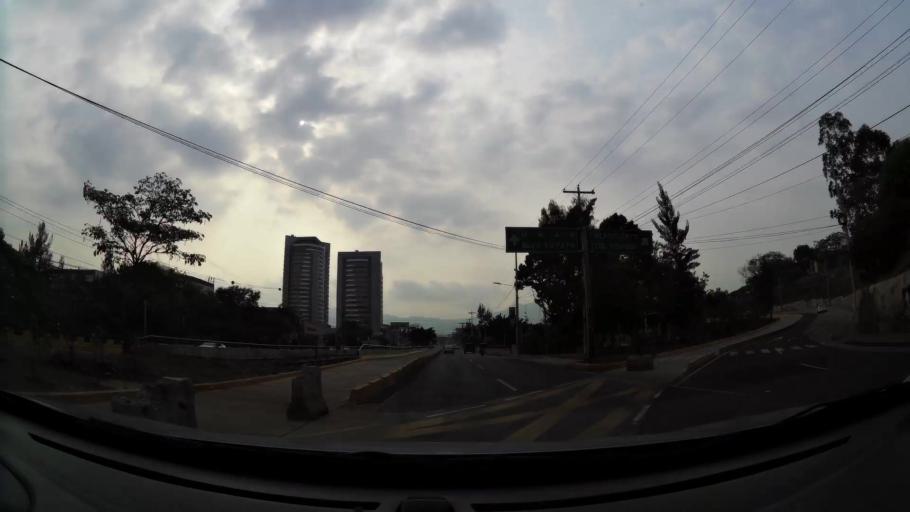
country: HN
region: Francisco Morazan
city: Tegucigalpa
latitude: 14.0858
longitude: -87.1891
